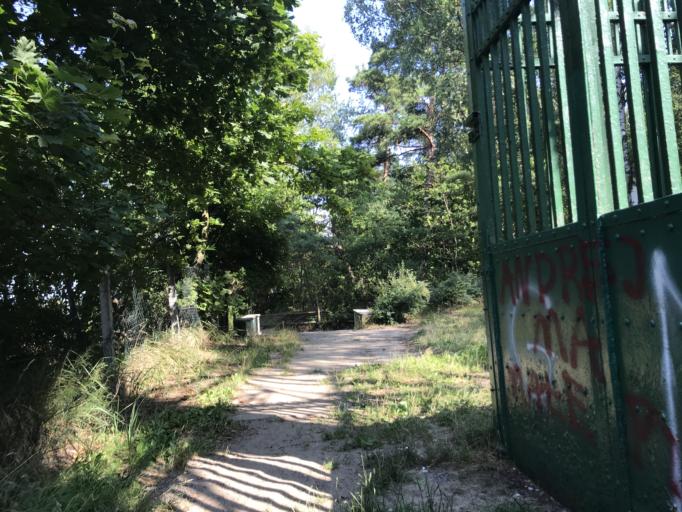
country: PL
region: Pomeranian Voivodeship
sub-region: Gdansk
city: Gdansk
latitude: 54.4087
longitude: 18.6402
